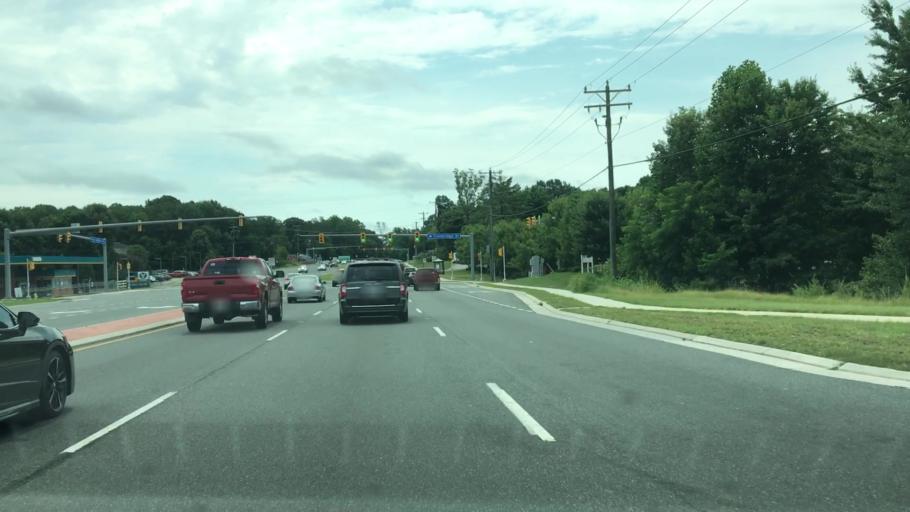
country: US
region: Virginia
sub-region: Prince William County
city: Dale City
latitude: 38.6661
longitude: -77.3318
